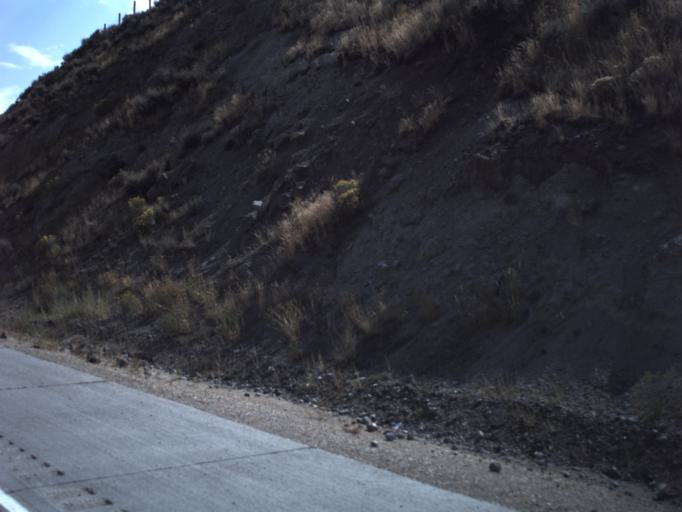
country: US
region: Utah
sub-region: Summit County
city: Snyderville
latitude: 40.7555
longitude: -111.4714
